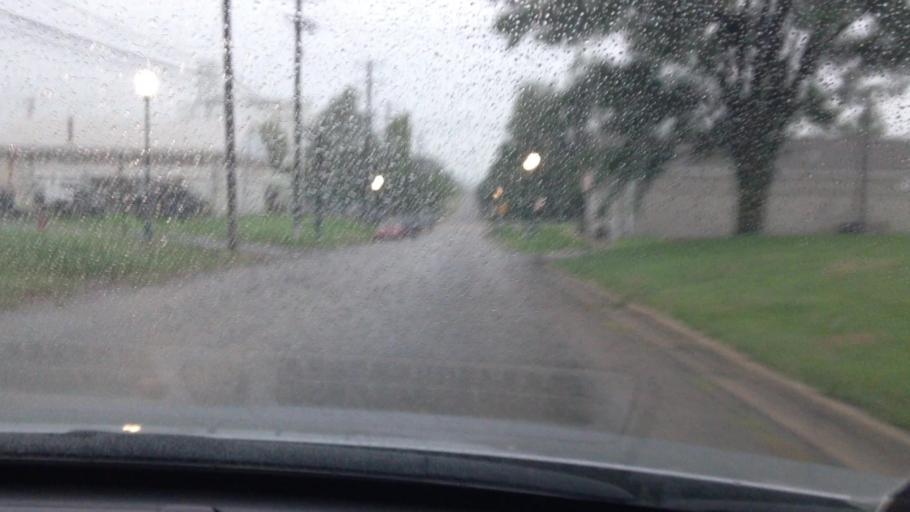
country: US
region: Kansas
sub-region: Brown County
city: Hiawatha
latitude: 39.8501
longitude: -95.5459
